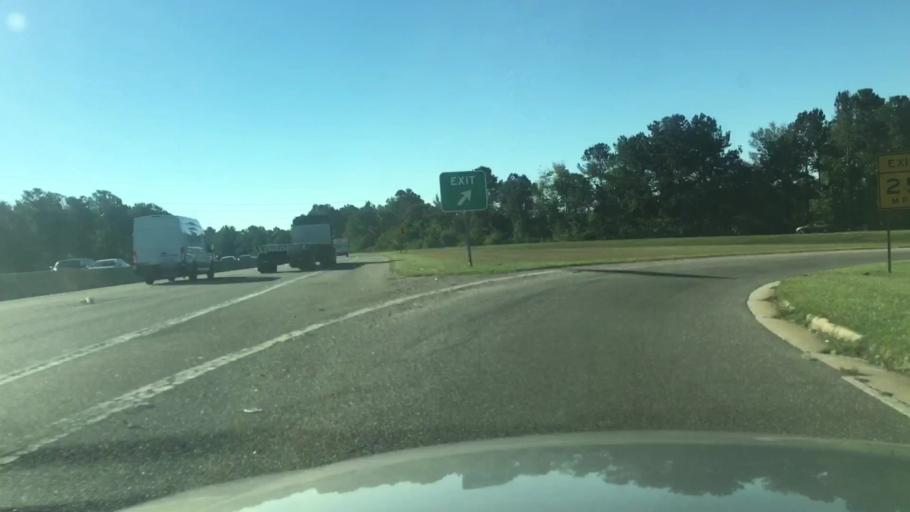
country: US
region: North Carolina
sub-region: Cumberland County
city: Fayetteville
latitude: 35.0435
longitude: -78.9391
